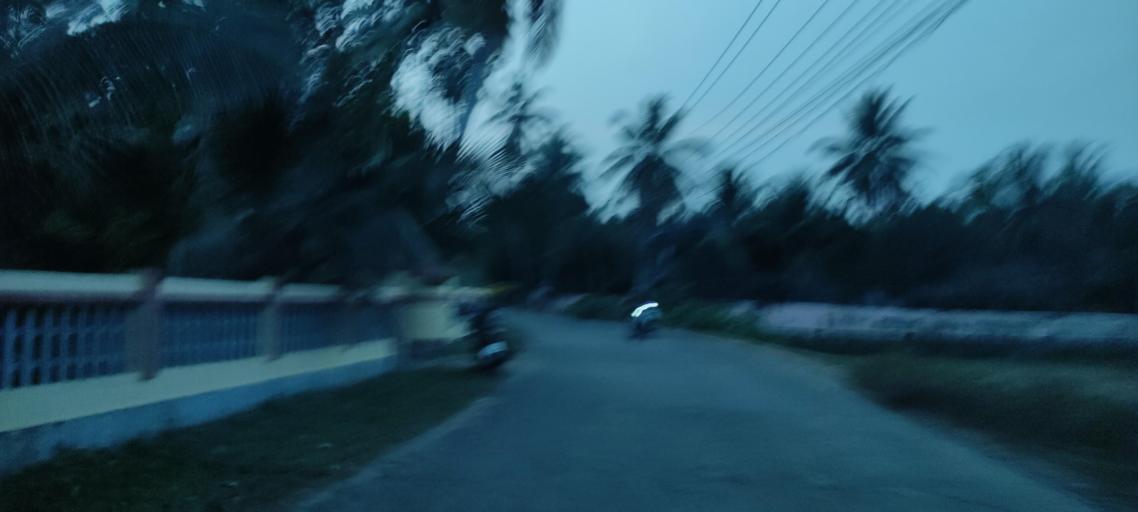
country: IN
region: Kerala
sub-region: Alappuzha
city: Mavelikara
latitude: 9.3308
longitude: 76.4874
